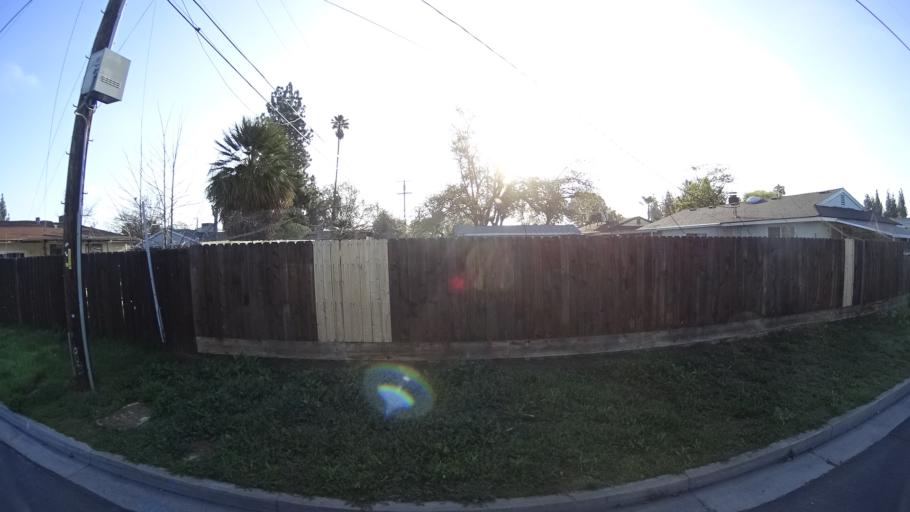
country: US
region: California
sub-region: Fresno County
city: Fresno
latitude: 36.8107
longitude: -119.7791
